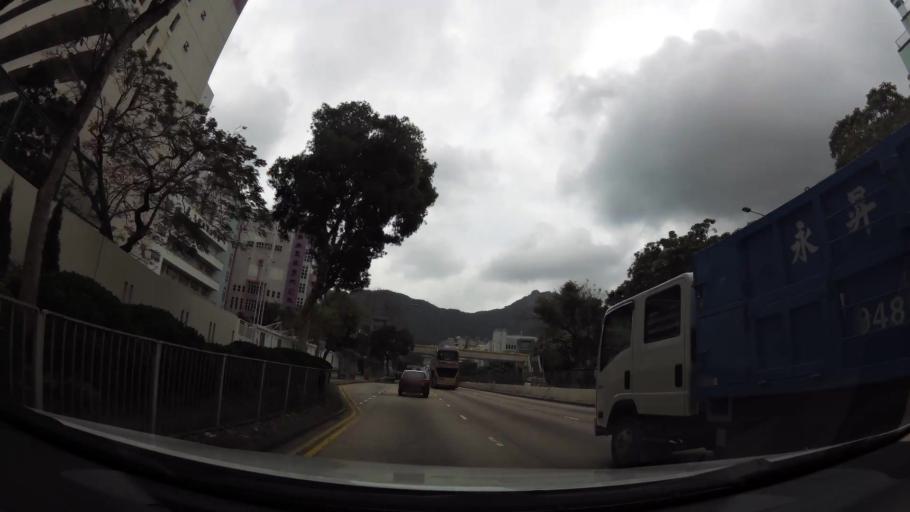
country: HK
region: Wong Tai Sin
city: Wong Tai Sin
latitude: 22.3355
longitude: 114.1789
